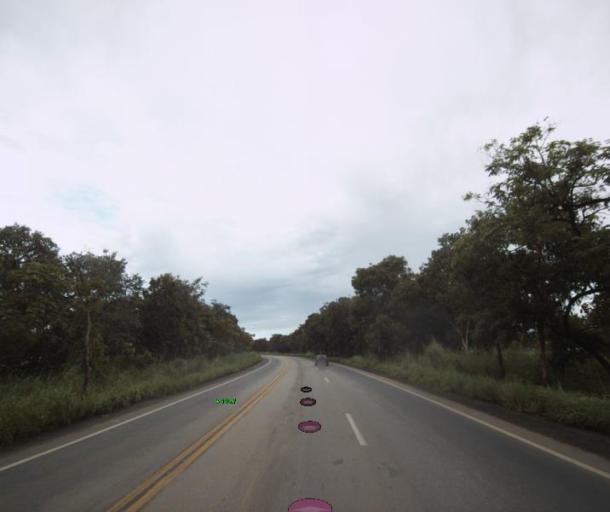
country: BR
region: Goias
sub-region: Porangatu
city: Porangatu
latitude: -13.7436
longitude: -49.0309
